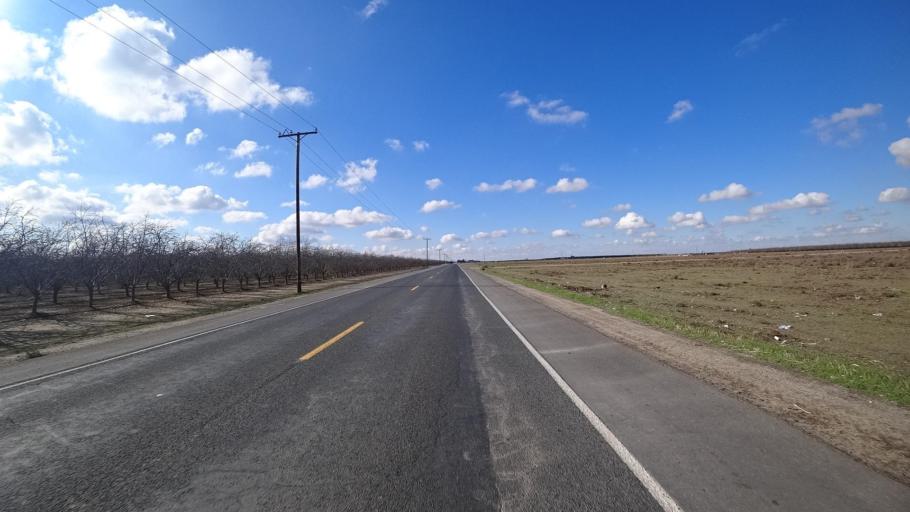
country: US
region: California
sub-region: Kern County
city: McFarland
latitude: 35.7179
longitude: -119.2441
